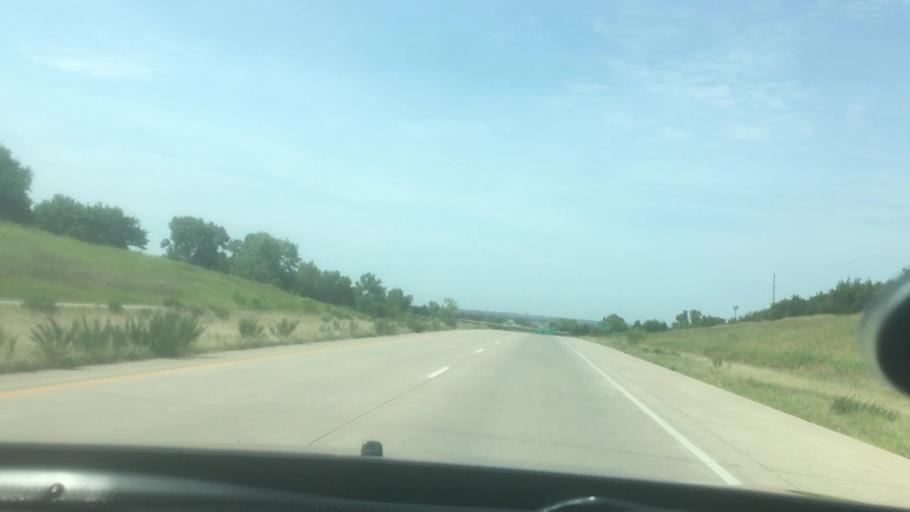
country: US
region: Oklahoma
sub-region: Pontotoc County
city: Ada
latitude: 34.7836
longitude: -96.6975
